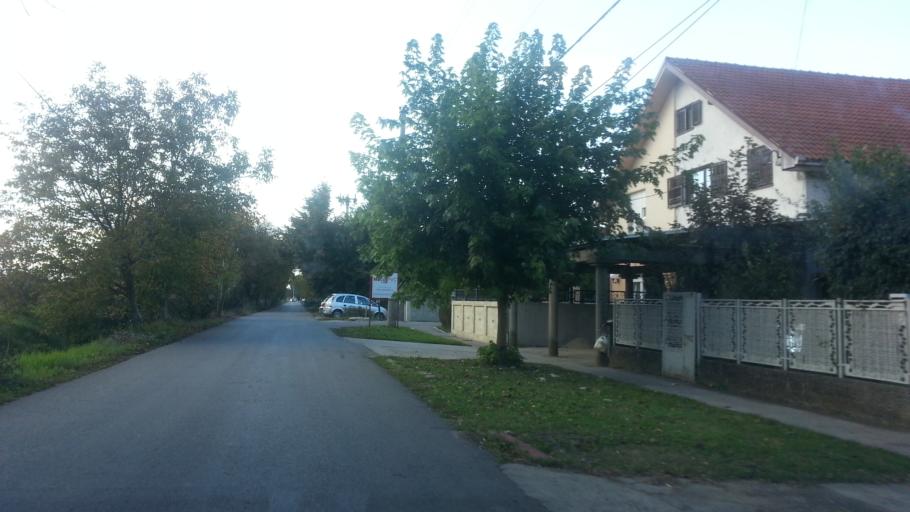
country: RS
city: Novi Banovci
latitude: 44.9041
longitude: 20.2643
